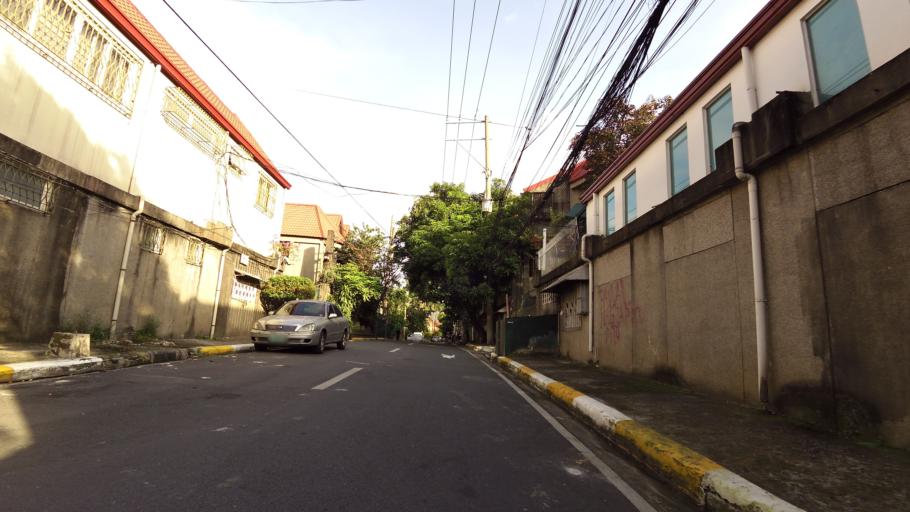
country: PH
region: Metro Manila
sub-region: San Juan
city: San Juan
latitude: 14.6082
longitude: 121.0351
